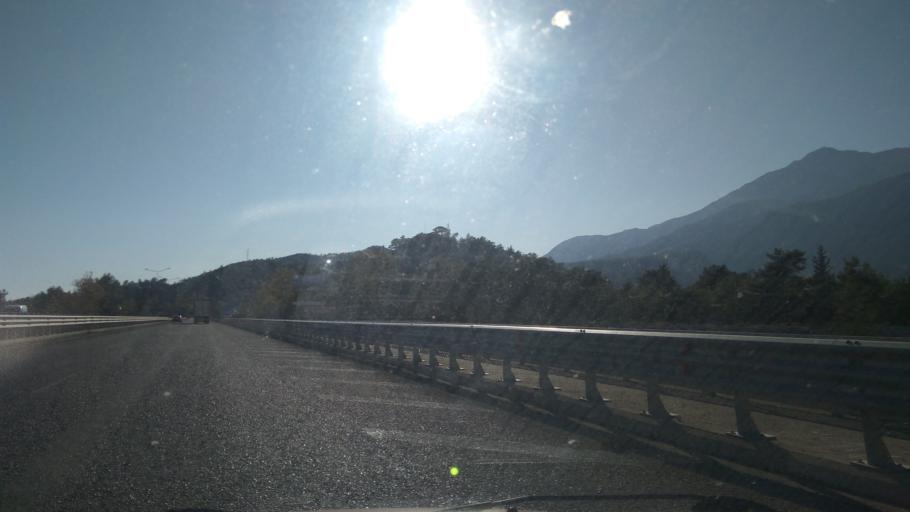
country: TR
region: Antalya
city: Kemer
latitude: 36.5755
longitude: 30.5553
